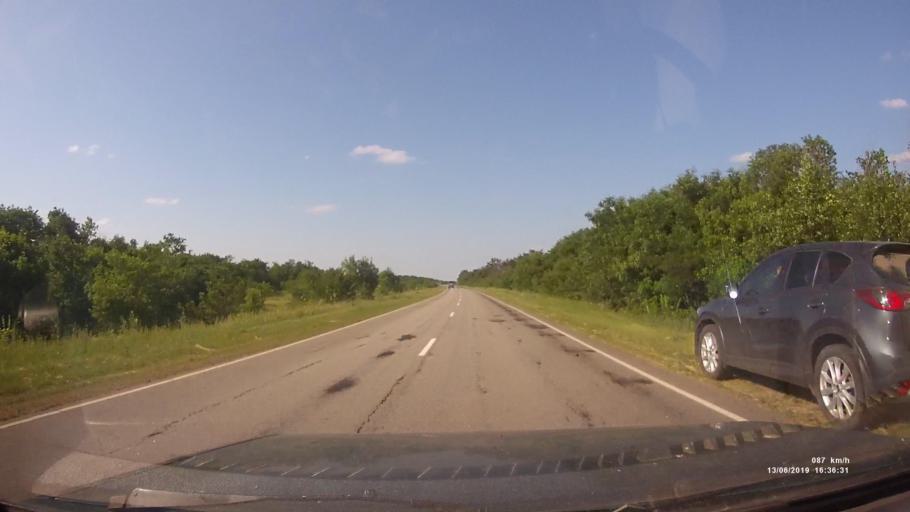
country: RU
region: Rostov
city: Kazanskaya
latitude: 49.8960
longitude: 41.3065
